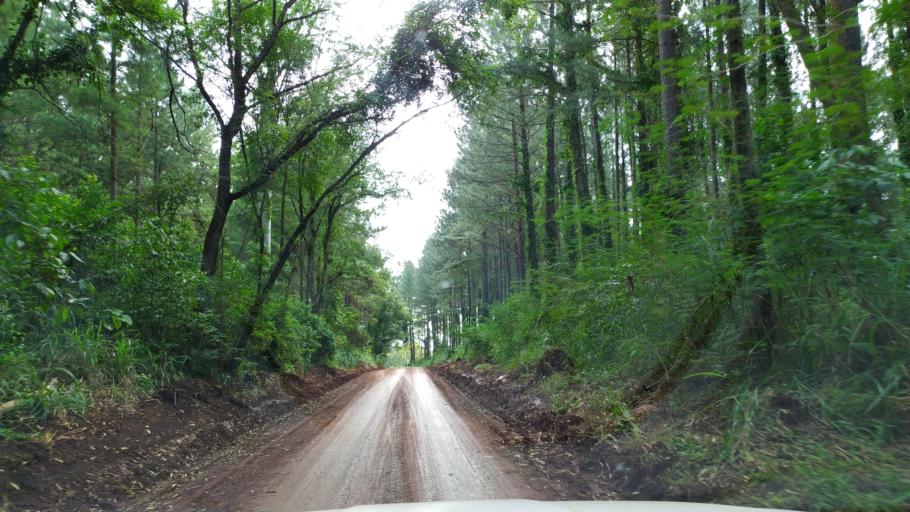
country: AR
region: Misiones
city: Puerto Piray
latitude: -26.5346
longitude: -54.6358
